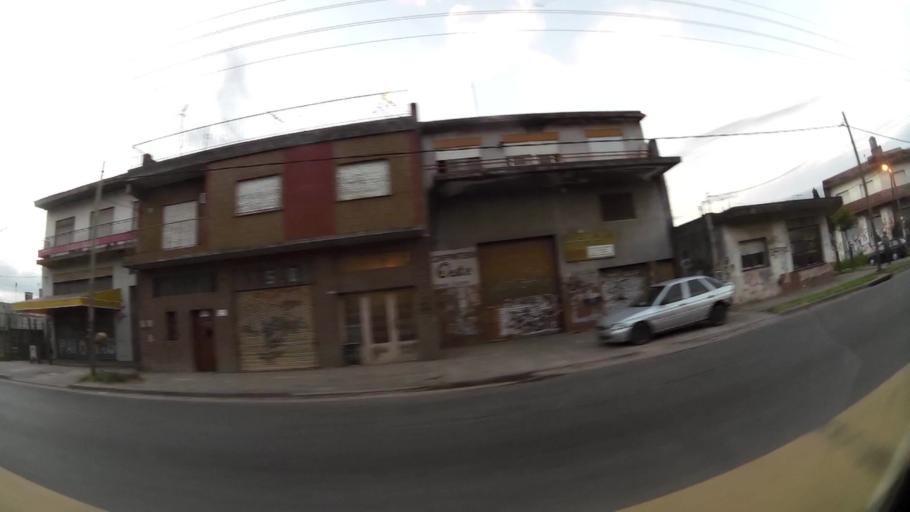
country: AR
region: Buenos Aires
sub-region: Partido de Merlo
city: Merlo
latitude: -34.6787
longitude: -58.7574
